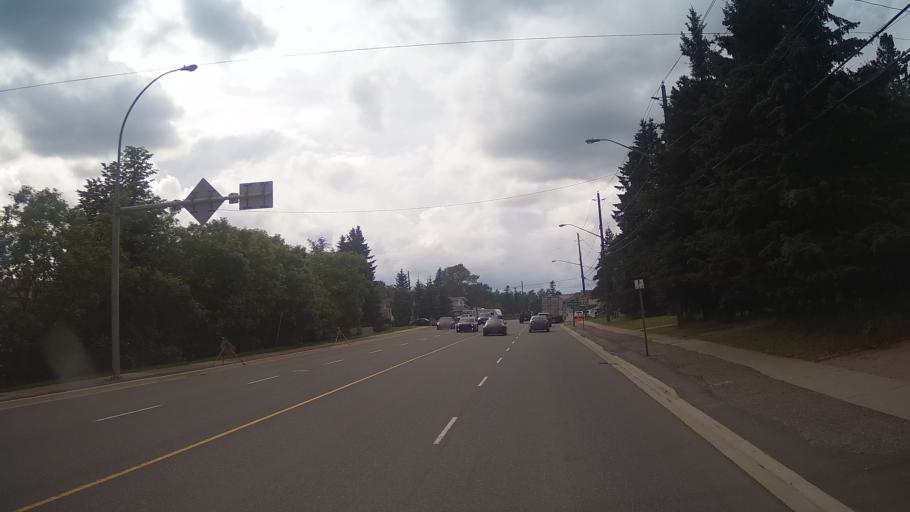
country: CA
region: Ontario
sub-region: Thunder Bay District
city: Thunder Bay
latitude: 48.4542
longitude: -89.2608
